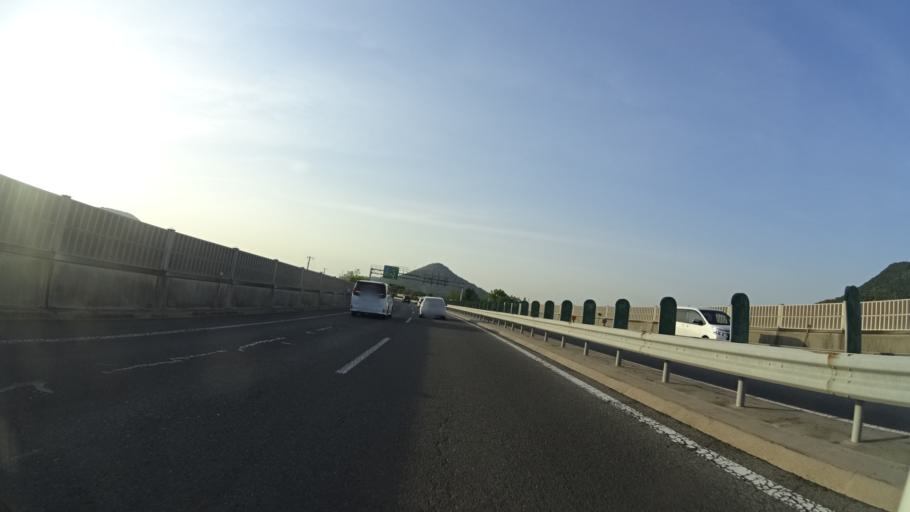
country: JP
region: Kagawa
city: Sakaidecho
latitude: 34.2882
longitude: 133.8513
